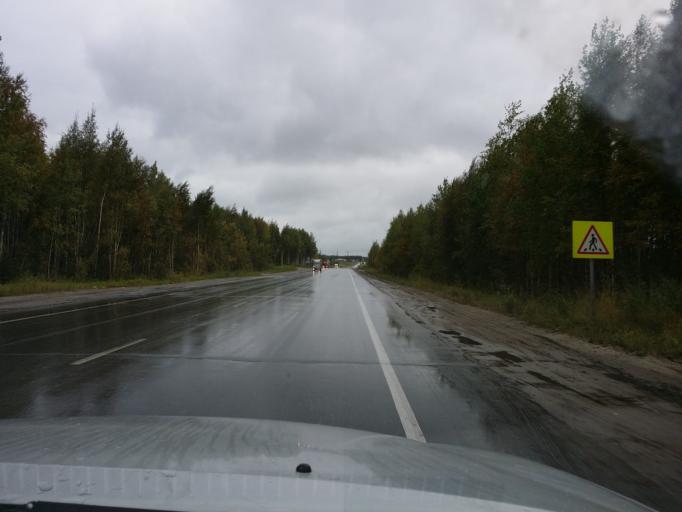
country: RU
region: Khanty-Mansiyskiy Avtonomnyy Okrug
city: Megion
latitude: 61.0654
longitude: 76.1154
